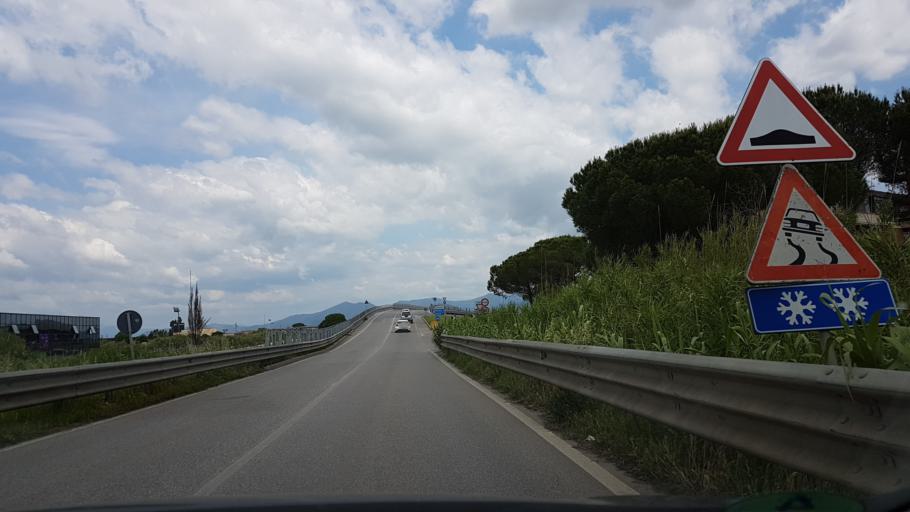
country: IT
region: Tuscany
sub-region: Provincia di Livorno
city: Collesalvetti
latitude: 43.5969
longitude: 10.4730
